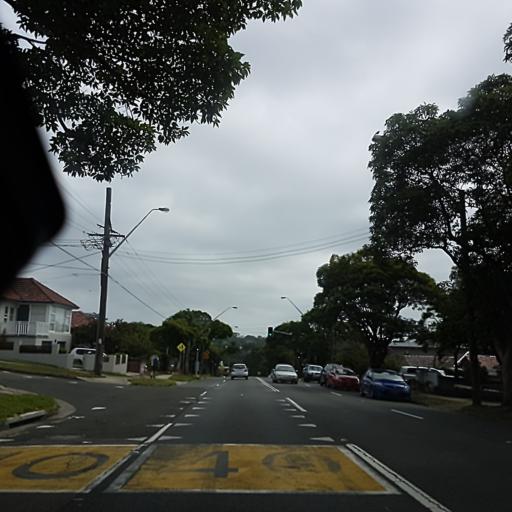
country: AU
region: New South Wales
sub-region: Manly Vale
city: Balgowlah
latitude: -33.7956
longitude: 151.2501
